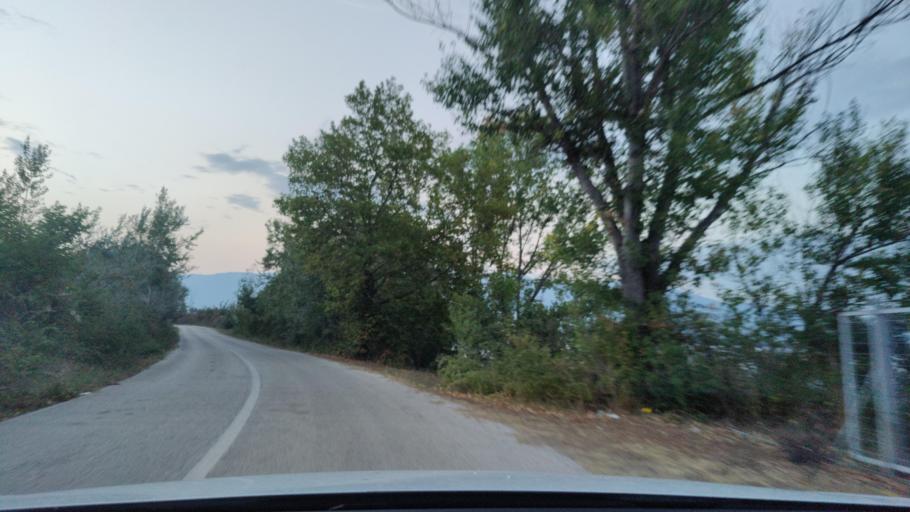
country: GR
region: Central Macedonia
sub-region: Nomos Serron
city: Chrysochorafa
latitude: 41.1460
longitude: 23.2128
